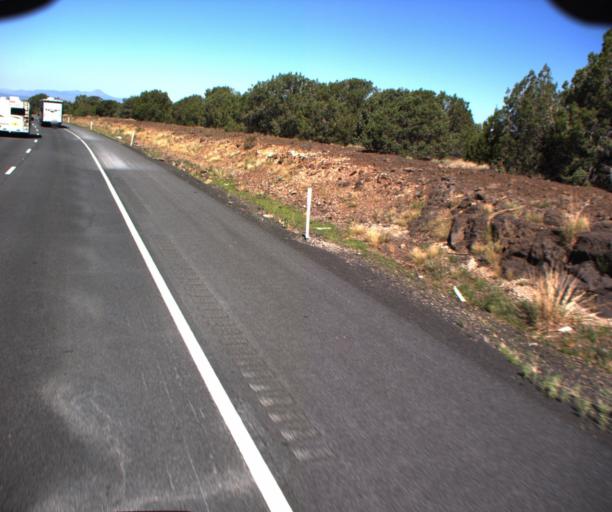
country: US
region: Arizona
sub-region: Coconino County
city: Williams
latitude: 35.2172
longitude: -112.3714
